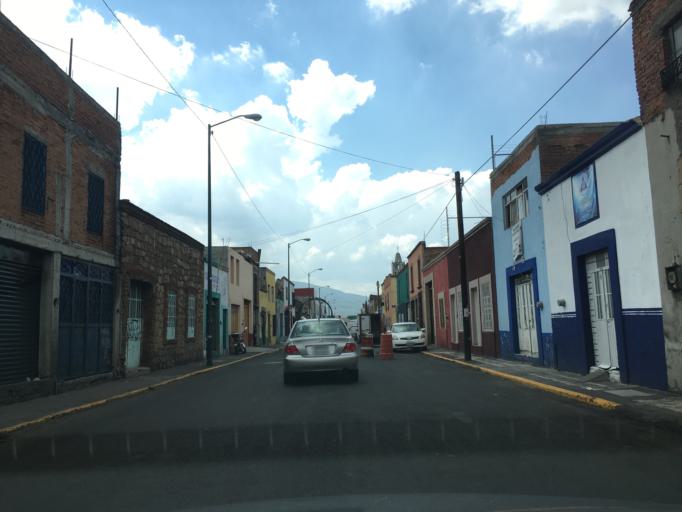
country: MX
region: Michoacan
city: Morelia
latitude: 19.7003
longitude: -101.2026
